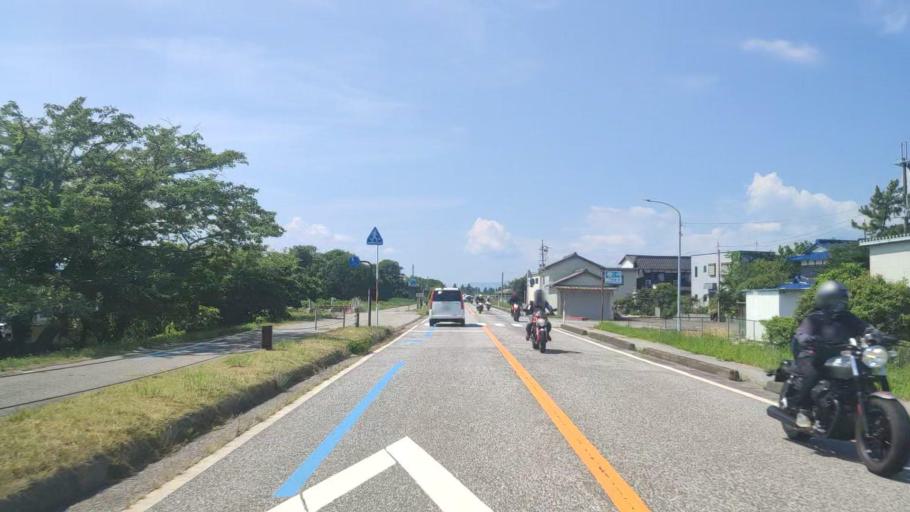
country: JP
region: Shiga Prefecture
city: Nagahama
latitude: 35.4022
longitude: 136.2158
